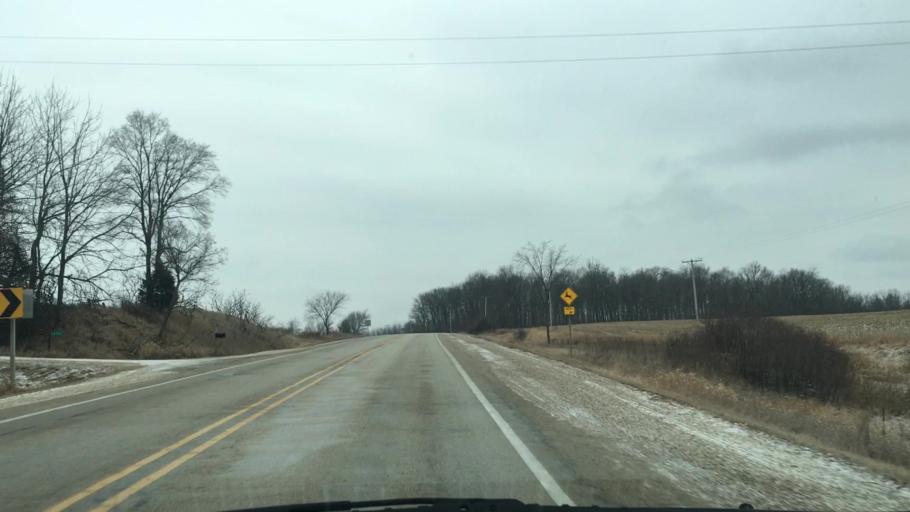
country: US
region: Iowa
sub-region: Fayette County
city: West Union
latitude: 43.0394
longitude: -91.8368
